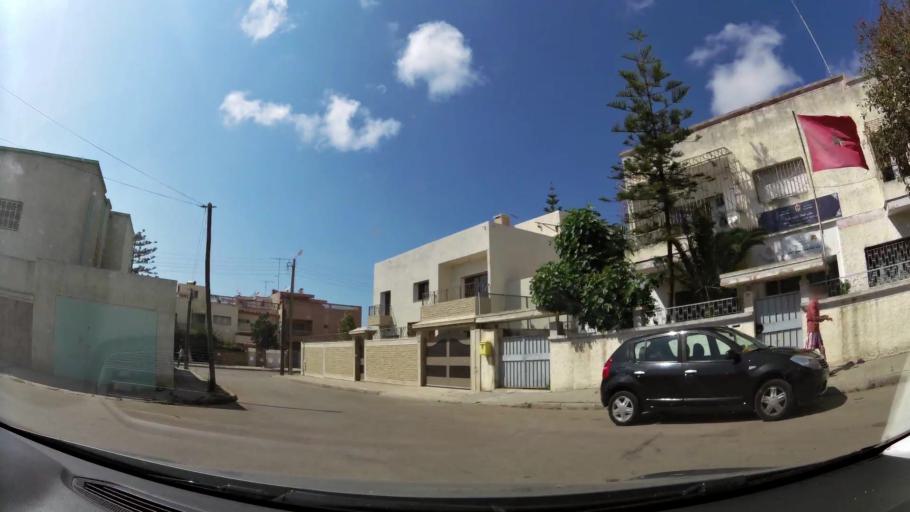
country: MA
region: Rabat-Sale-Zemmour-Zaer
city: Sale
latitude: 34.0368
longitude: -6.7881
